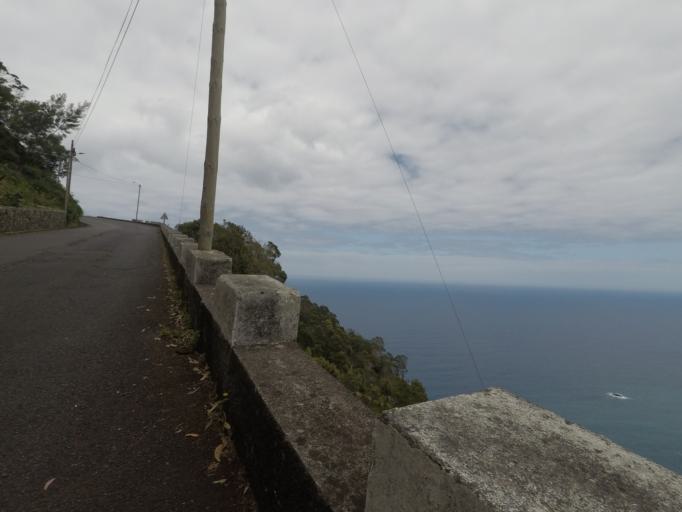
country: PT
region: Madeira
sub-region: Santana
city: Santana
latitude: 32.7939
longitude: -16.8627
